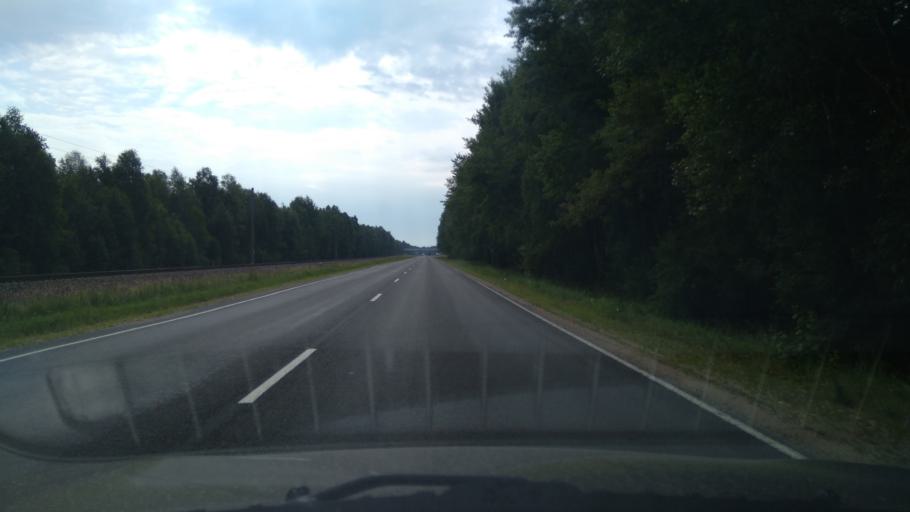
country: BY
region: Brest
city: Nyakhachava
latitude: 52.5825
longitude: 25.1024
